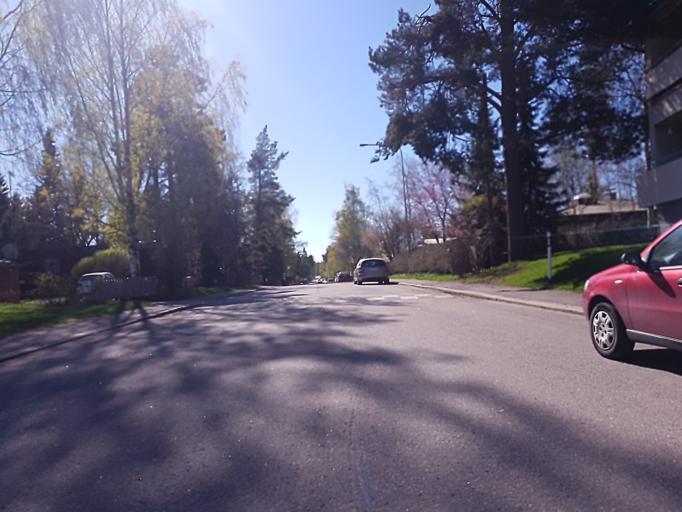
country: FI
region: Uusimaa
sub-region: Helsinki
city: Helsinki
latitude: 60.2453
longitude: 24.9283
